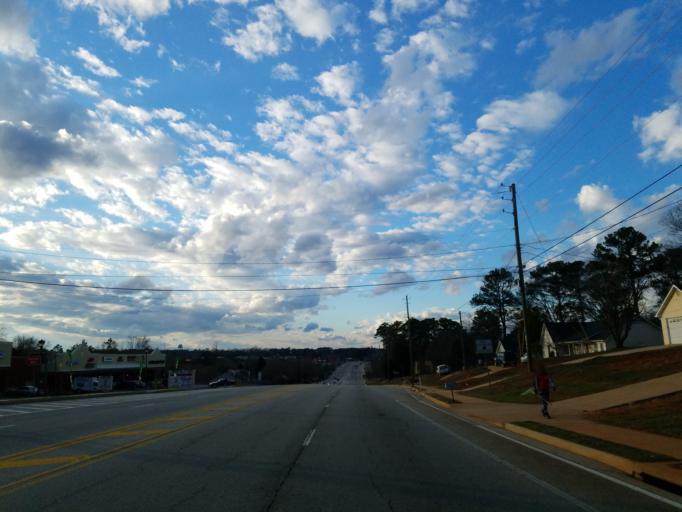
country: US
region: Georgia
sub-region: Henry County
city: McDonough
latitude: 33.4493
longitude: -84.1597
